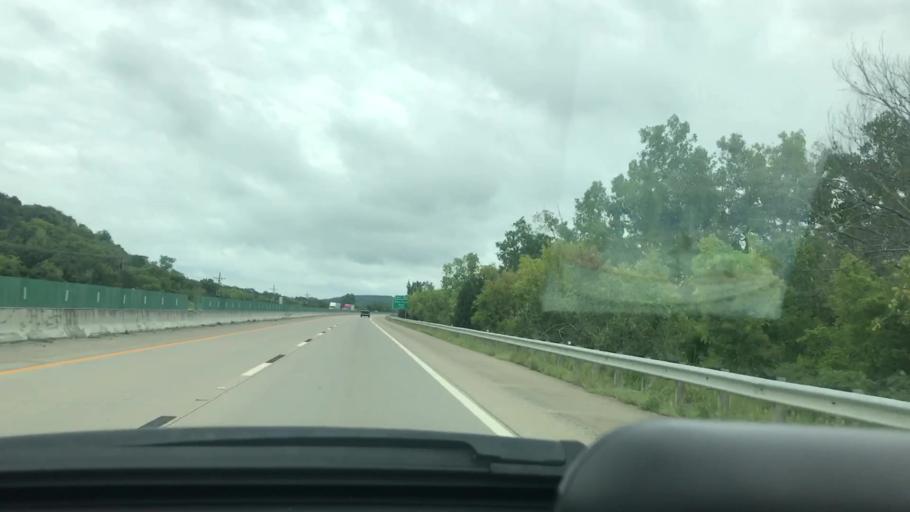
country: US
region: Oklahoma
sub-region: Pittsburg County
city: Krebs
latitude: 35.0907
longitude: -95.7003
